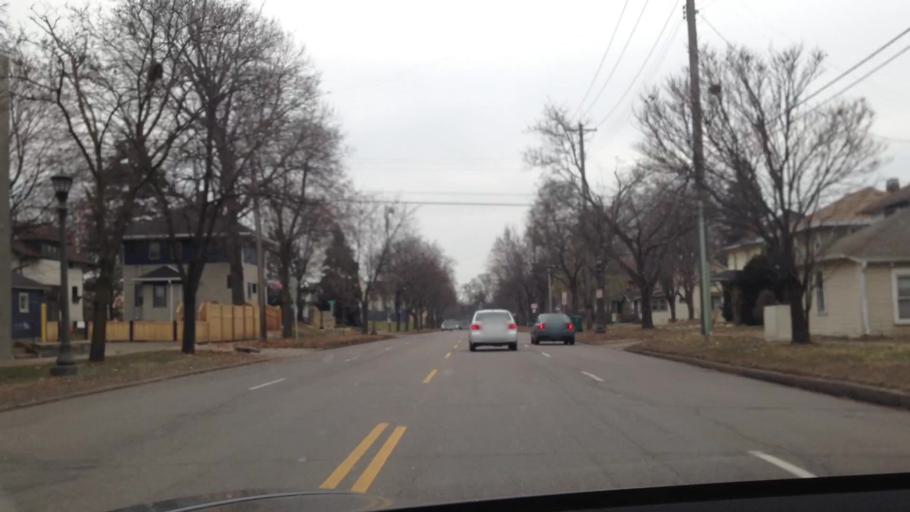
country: US
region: Minnesota
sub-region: Ramsey County
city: Falcon Heights
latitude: 44.9471
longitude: -93.1924
